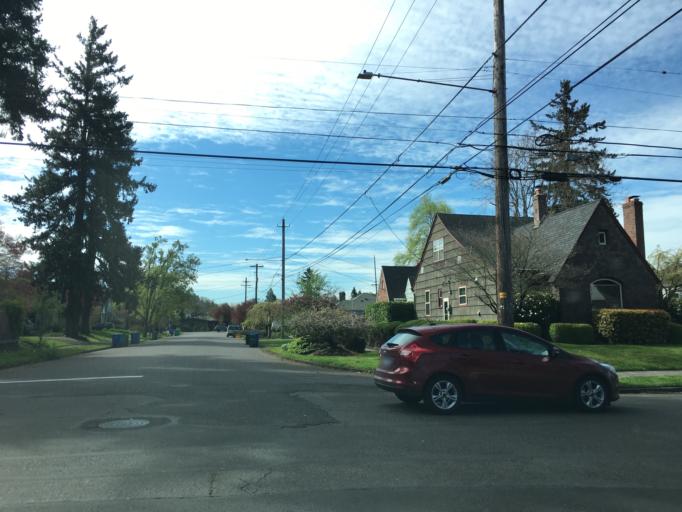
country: US
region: Oregon
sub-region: Multnomah County
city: Lents
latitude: 45.5350
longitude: -122.5996
